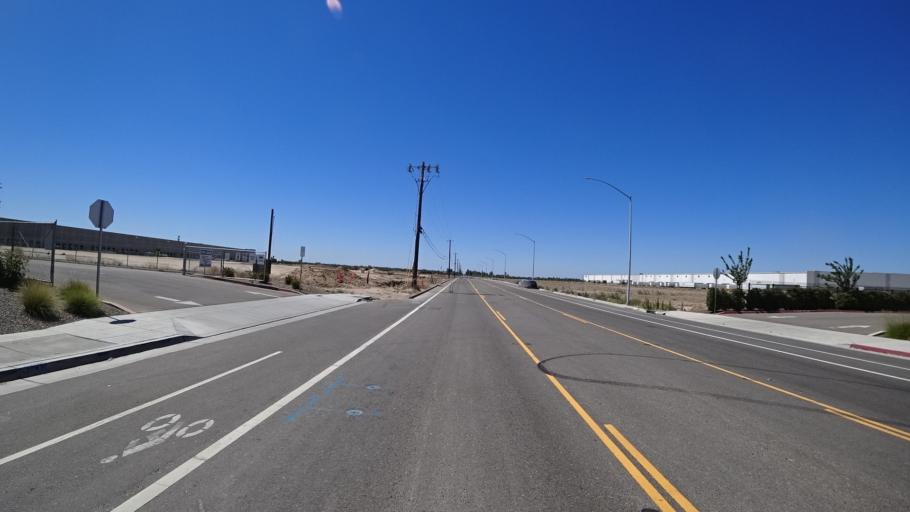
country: US
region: California
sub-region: Fresno County
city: Easton
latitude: 36.6834
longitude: -119.7727
